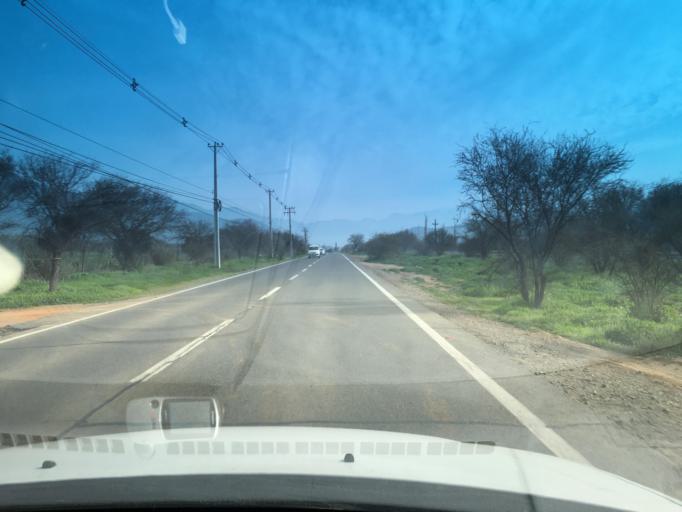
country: CL
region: Santiago Metropolitan
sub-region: Provincia de Chacabuco
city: Lampa
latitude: -33.1570
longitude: -70.8993
